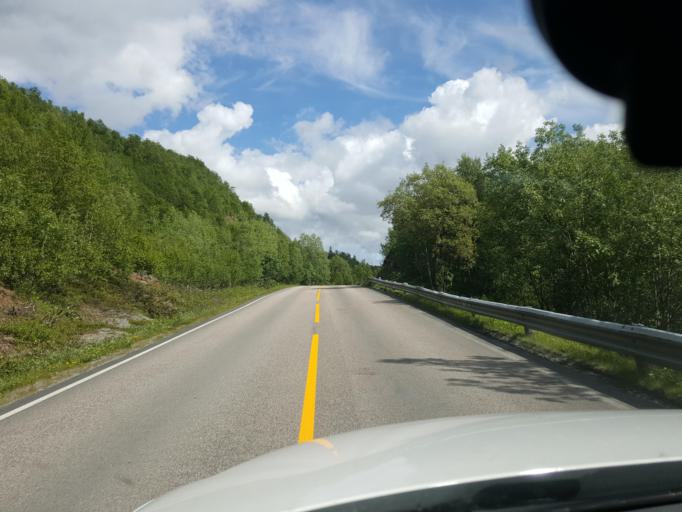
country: NO
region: Nordland
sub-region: Rana
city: Mo i Rana
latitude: 66.2879
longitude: 14.4340
